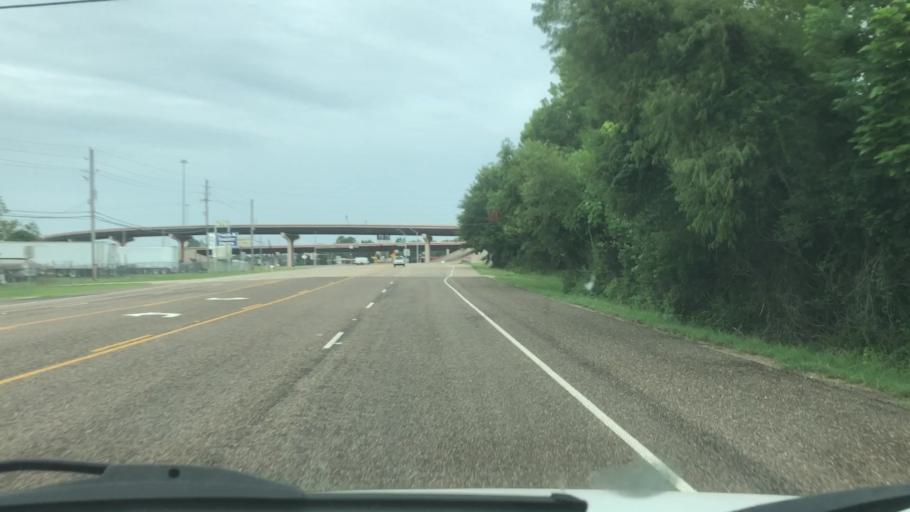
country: US
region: Texas
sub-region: Bowie County
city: Wake Village
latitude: 33.3962
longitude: -94.0944
